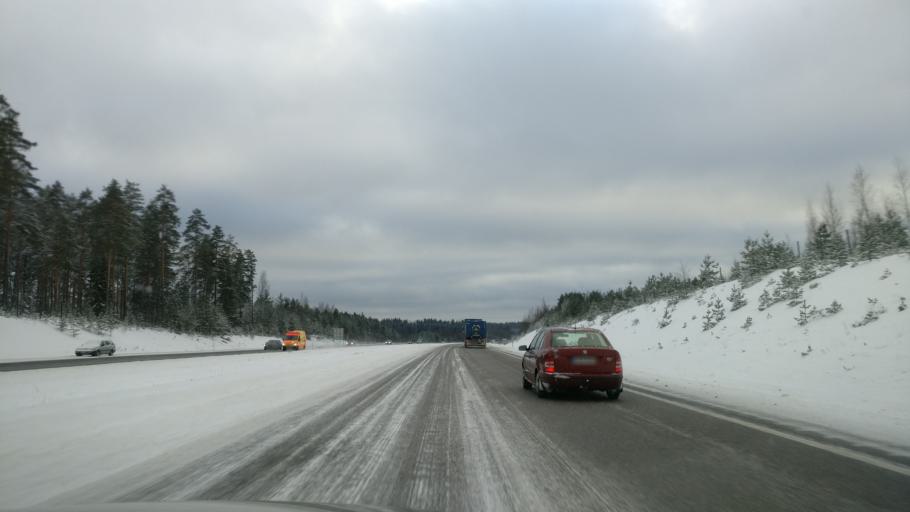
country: FI
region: Paijanne Tavastia
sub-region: Lahti
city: Nastola
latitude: 61.1050
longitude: 25.9139
